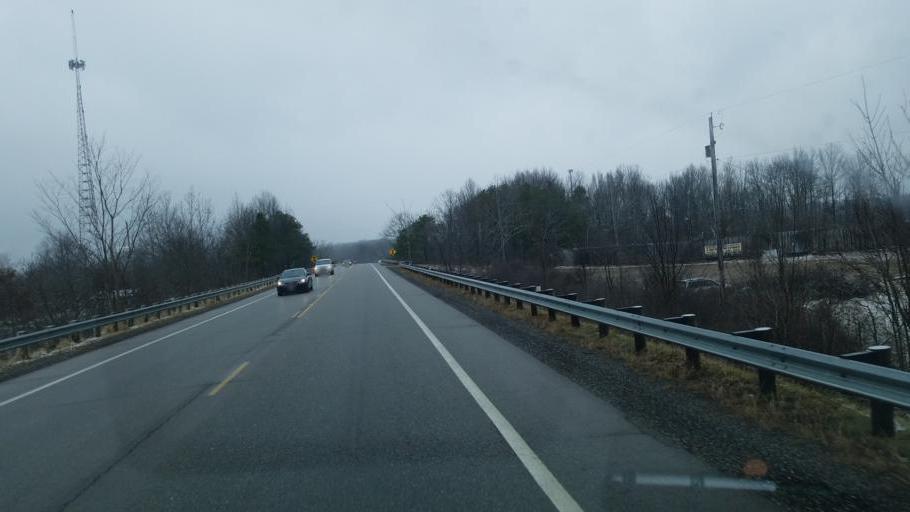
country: US
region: Ohio
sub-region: Portage County
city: Ravenna
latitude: 41.1722
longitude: -81.2264
